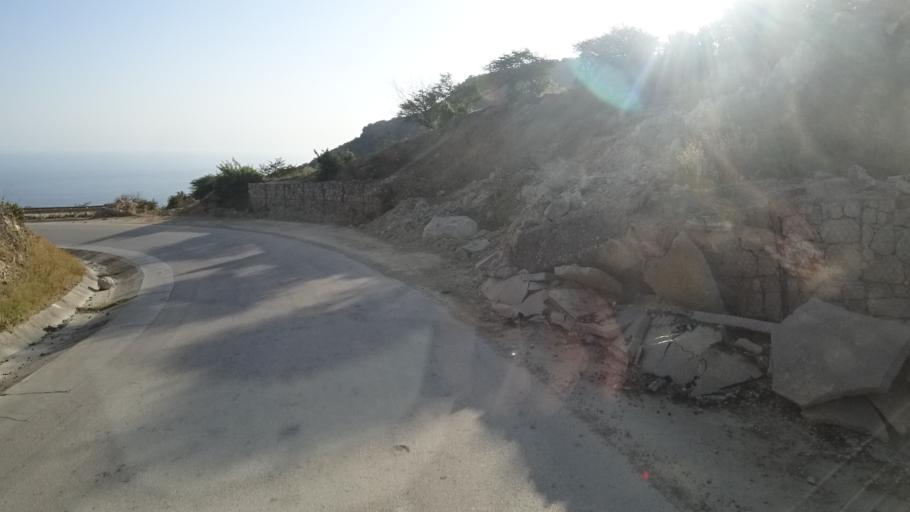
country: OM
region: Zufar
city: Salalah
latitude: 17.0586
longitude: 54.6099
